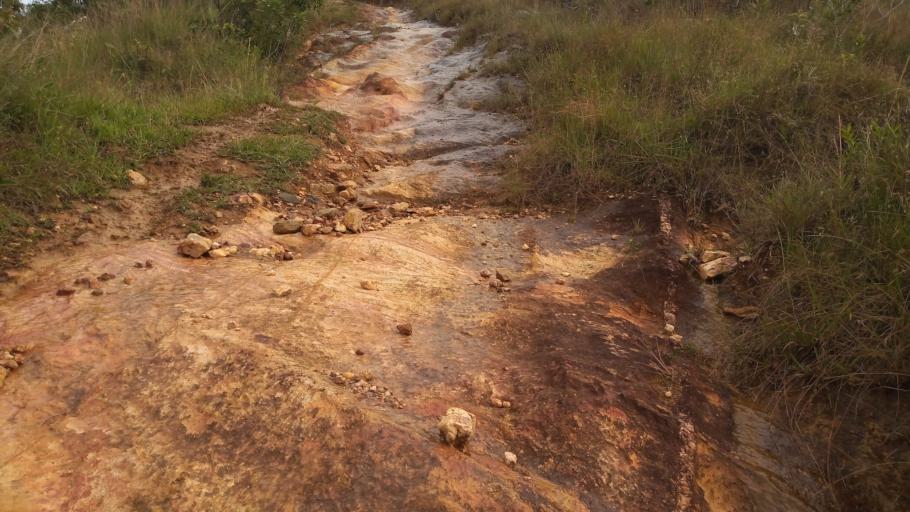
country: BR
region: Minas Gerais
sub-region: Sao Joao Del Rei
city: Sao Joao del Rei
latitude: -21.1228
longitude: -44.2740
